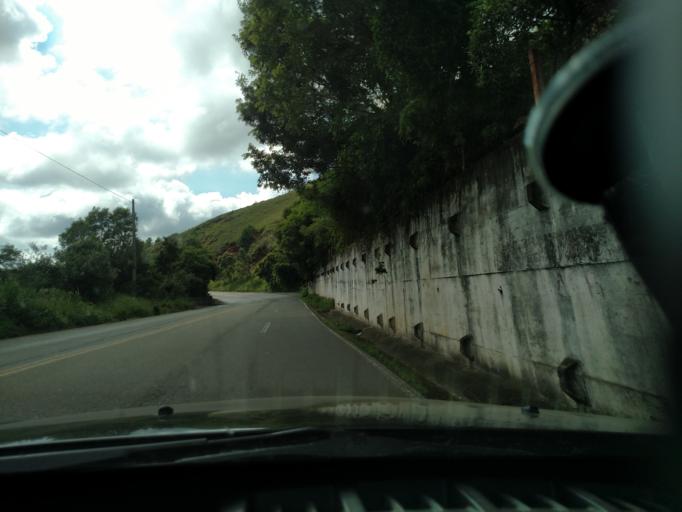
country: BR
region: Santa Catarina
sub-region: Lages
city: Lages
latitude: -27.8668
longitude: -50.1919
